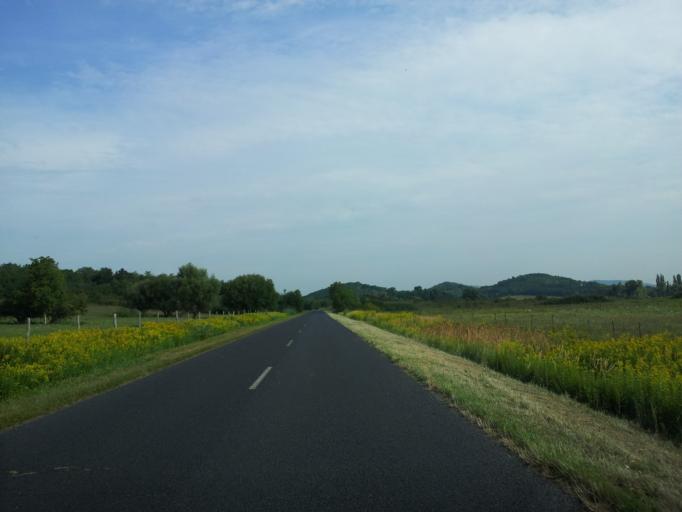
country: HU
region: Veszprem
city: Badacsonytomaj
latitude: 46.8426
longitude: 17.5514
